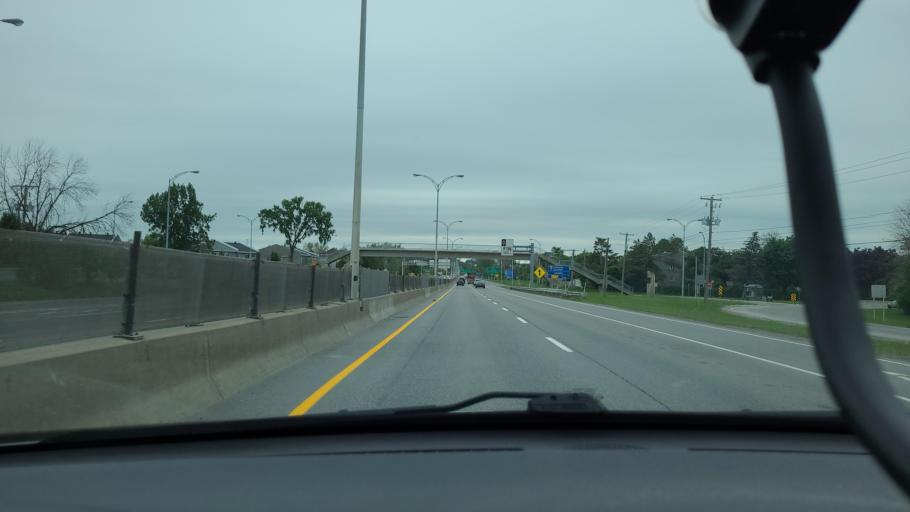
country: CA
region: Quebec
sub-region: Lanaudiere
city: Terrebonne
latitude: 45.6910
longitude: -73.6506
